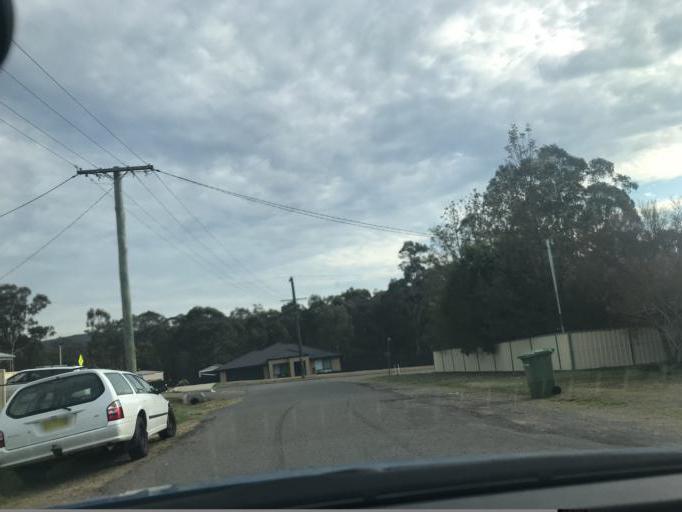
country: AU
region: New South Wales
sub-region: Cessnock
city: Cessnock
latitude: -32.9024
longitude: 151.2859
